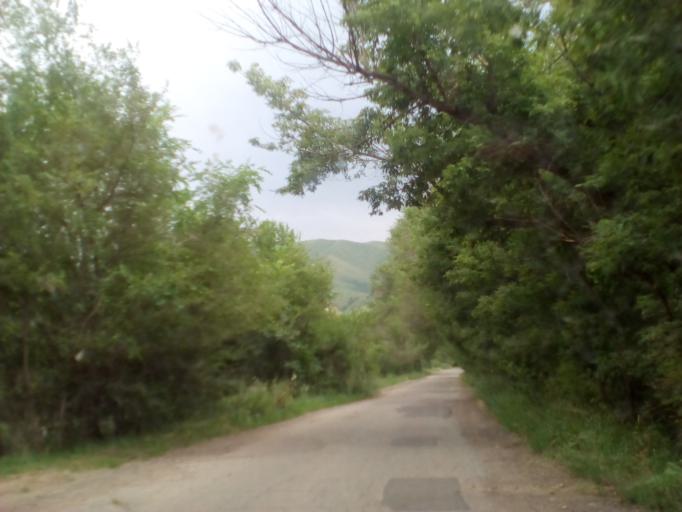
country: KZ
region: Almaty Oblysy
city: Burunday
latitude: 43.1627
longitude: 76.3872
